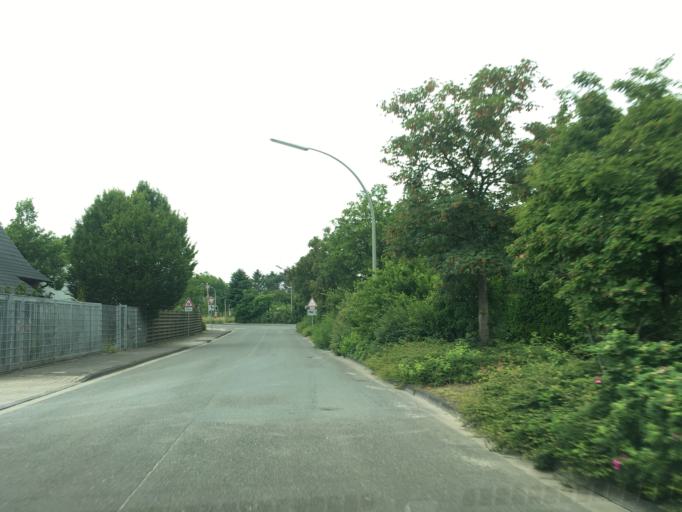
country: DE
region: North Rhine-Westphalia
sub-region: Regierungsbezirk Munster
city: Steinfurt
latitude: 52.1549
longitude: 7.3206
